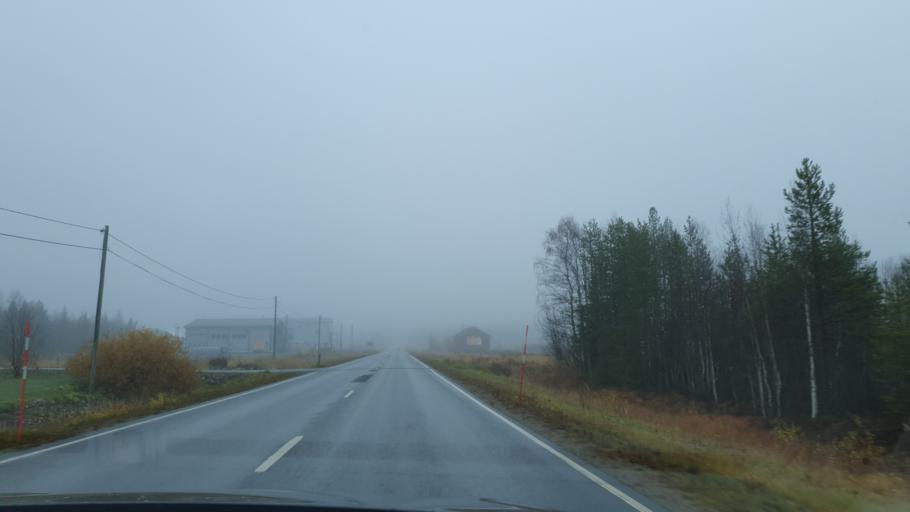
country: FI
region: Lapland
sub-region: Tunturi-Lappi
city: Kittilae
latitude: 67.6670
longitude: 24.8618
